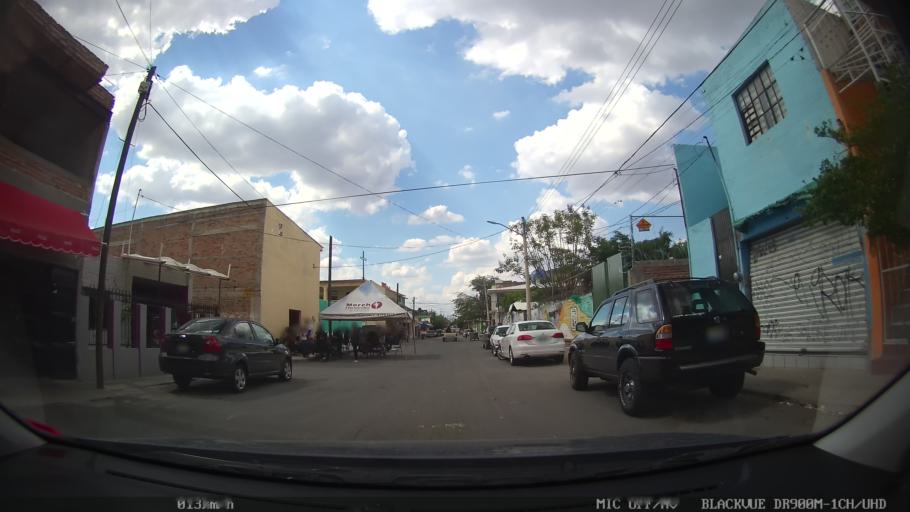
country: MX
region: Jalisco
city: Tlaquepaque
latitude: 20.6804
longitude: -103.2603
